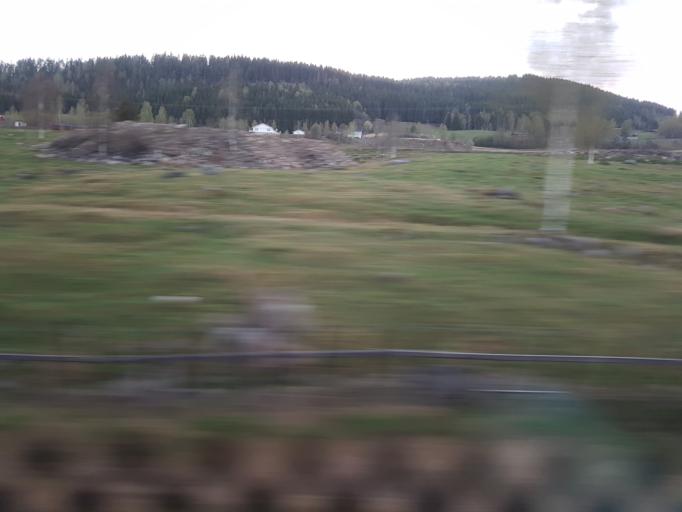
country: NO
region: Hedmark
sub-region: Ringsaker
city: Moelv
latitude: 60.9155
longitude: 10.7683
